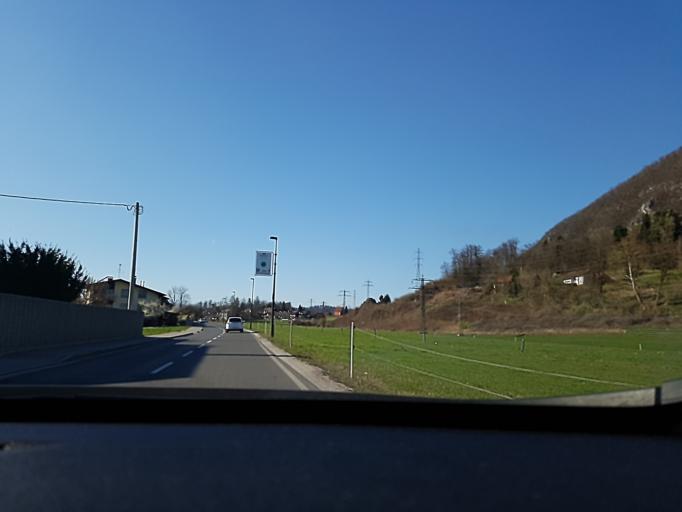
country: SI
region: Medvode
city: Zgornje Pirnice
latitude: 46.1204
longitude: 14.4490
